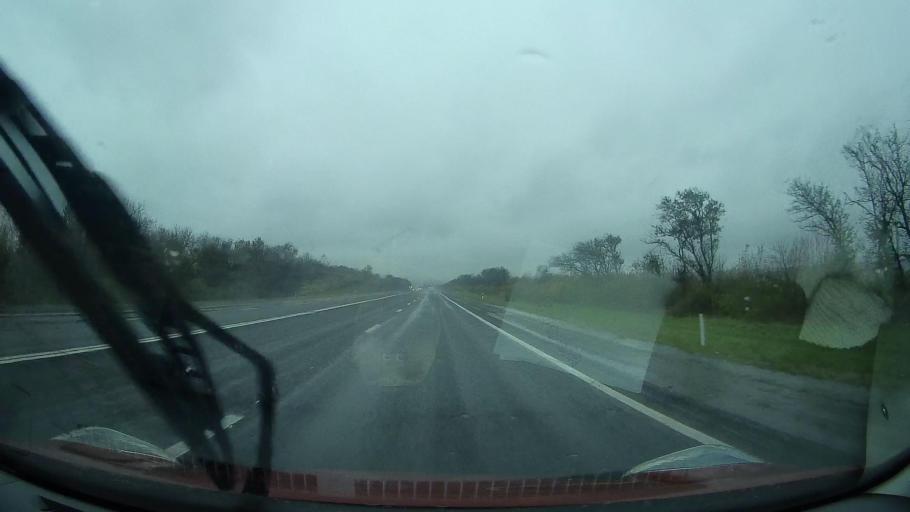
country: RU
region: Stavropol'skiy
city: Nevinnomyssk
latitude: 44.6172
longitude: 42.1018
